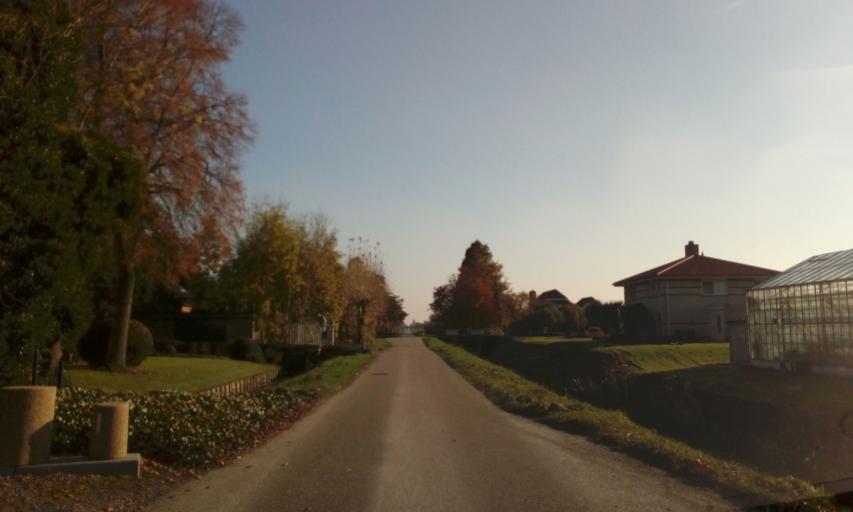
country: NL
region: South Holland
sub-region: Gemeente Waddinxveen
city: Groenswaard
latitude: 52.0111
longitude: 4.5973
